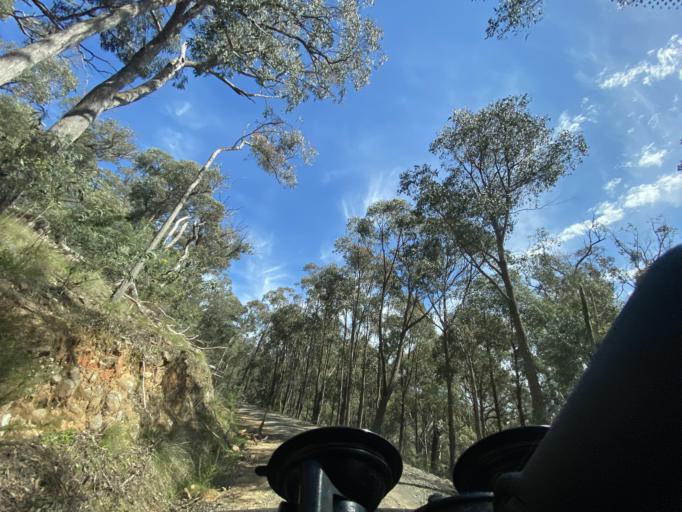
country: AU
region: Victoria
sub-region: Mansfield
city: Mansfield
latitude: -36.8105
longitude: 146.1023
